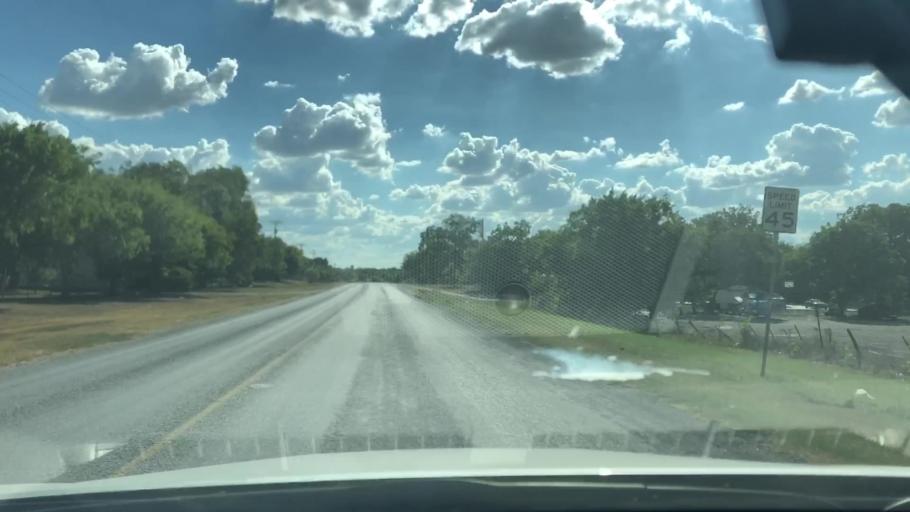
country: US
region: Texas
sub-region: Comal County
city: New Braunfels
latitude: 29.6691
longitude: -98.1654
